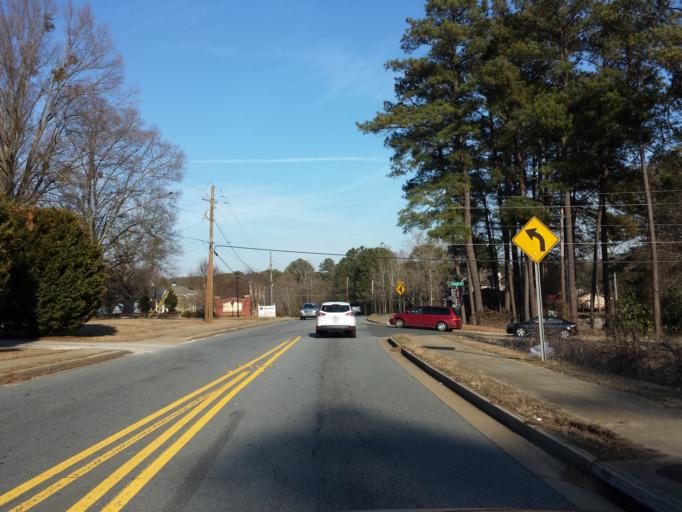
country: US
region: Georgia
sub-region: Cherokee County
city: Woodstock
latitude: 34.0327
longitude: -84.5256
